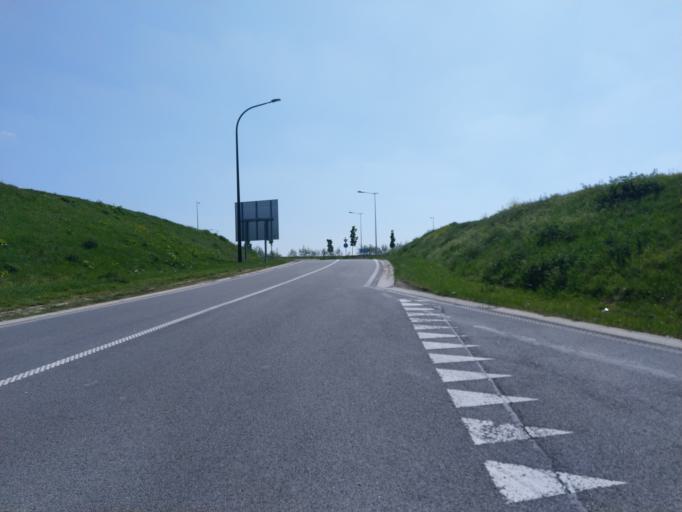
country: BE
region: Wallonia
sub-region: Province du Hainaut
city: Soignies
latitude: 50.5920
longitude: 4.0790
